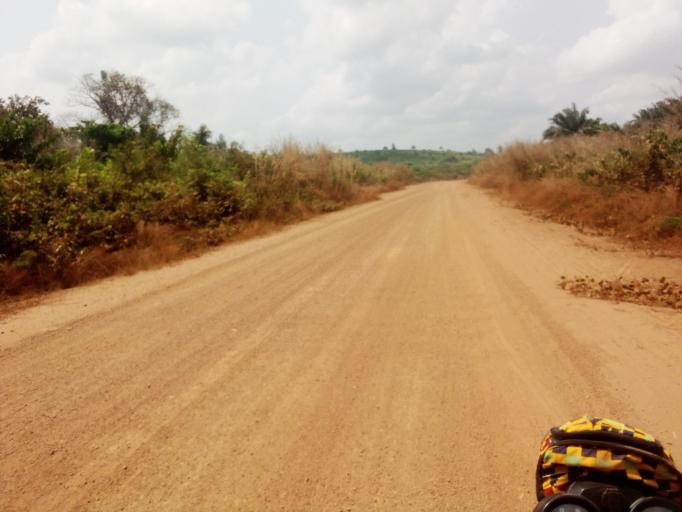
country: SL
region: Southern Province
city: Mogbwemo
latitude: 7.6605
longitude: -12.2641
